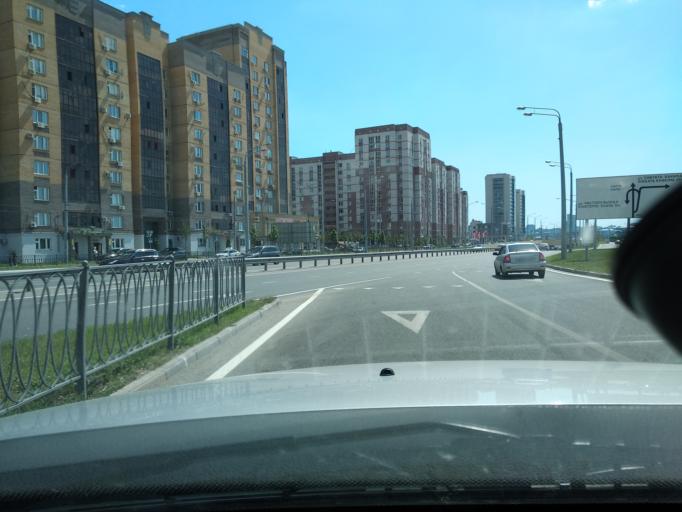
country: RU
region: Tatarstan
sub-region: Gorod Kazan'
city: Kazan
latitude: 55.8189
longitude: 49.1335
